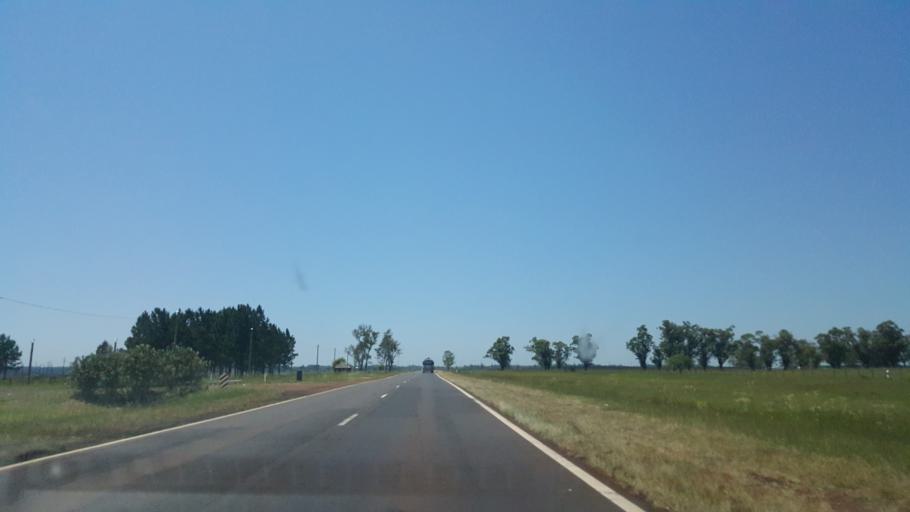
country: AR
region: Corrientes
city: Santo Tome
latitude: -28.5198
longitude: -56.1060
